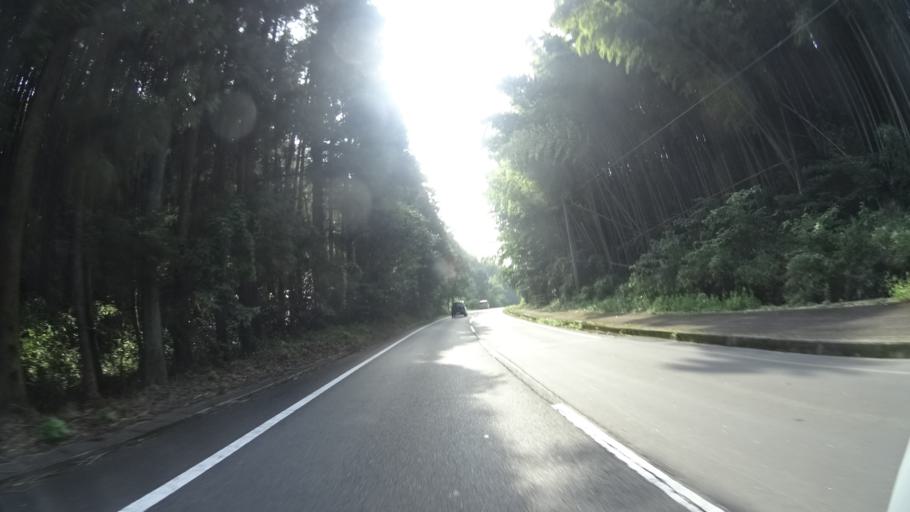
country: JP
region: Kagoshima
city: Okuchi-shinohara
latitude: 32.0177
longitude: 130.6266
